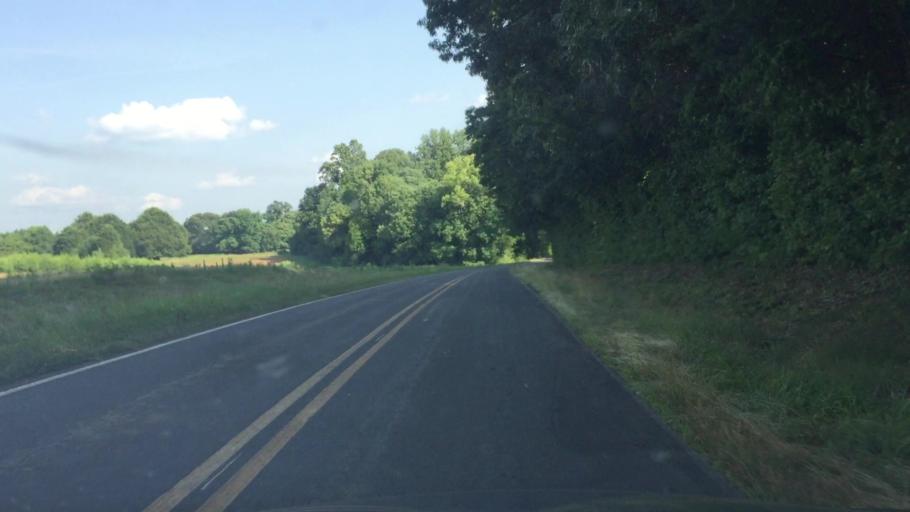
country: US
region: North Carolina
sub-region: Rockingham County
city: Reidsville
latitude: 36.2733
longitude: -79.5673
